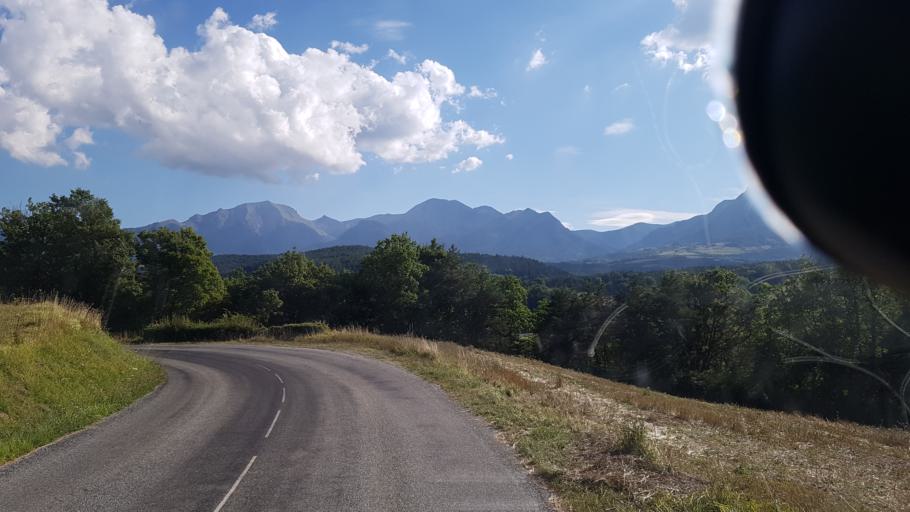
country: FR
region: Rhone-Alpes
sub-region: Departement de l'Isere
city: Mens
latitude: 44.8266
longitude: 5.6702
